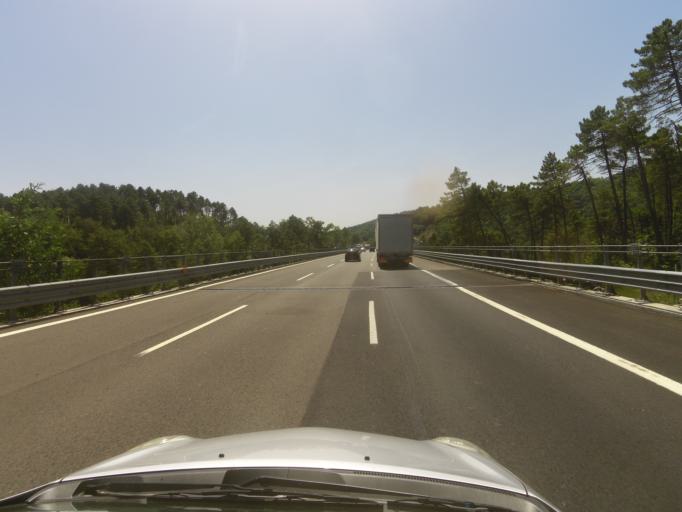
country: IT
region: Tuscany
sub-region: Province of Florence
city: Barberino di Mugello
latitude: 44.0137
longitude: 11.2203
